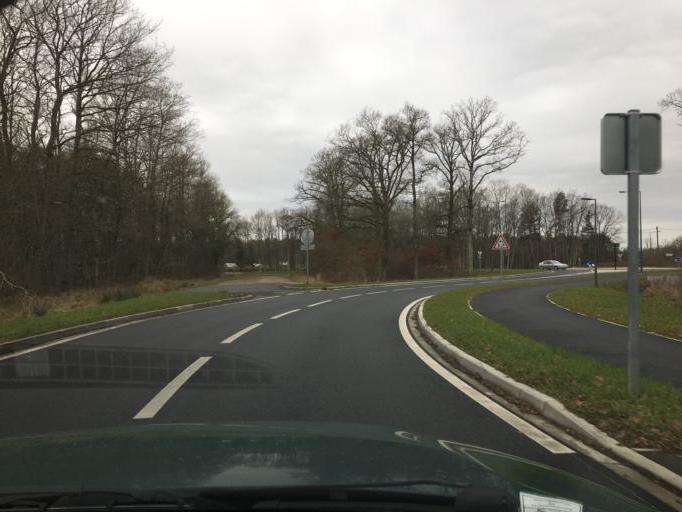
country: FR
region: Centre
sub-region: Departement du Loiret
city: Fleury-les-Aubrais
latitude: 47.9531
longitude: 1.9237
